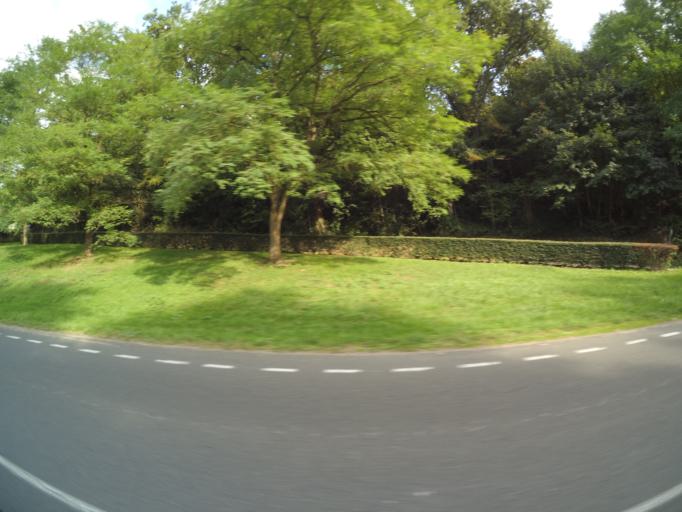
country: FR
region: Centre
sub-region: Departement d'Indre-et-Loire
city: Nazelles-Negron
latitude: 47.4348
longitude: 0.9541
